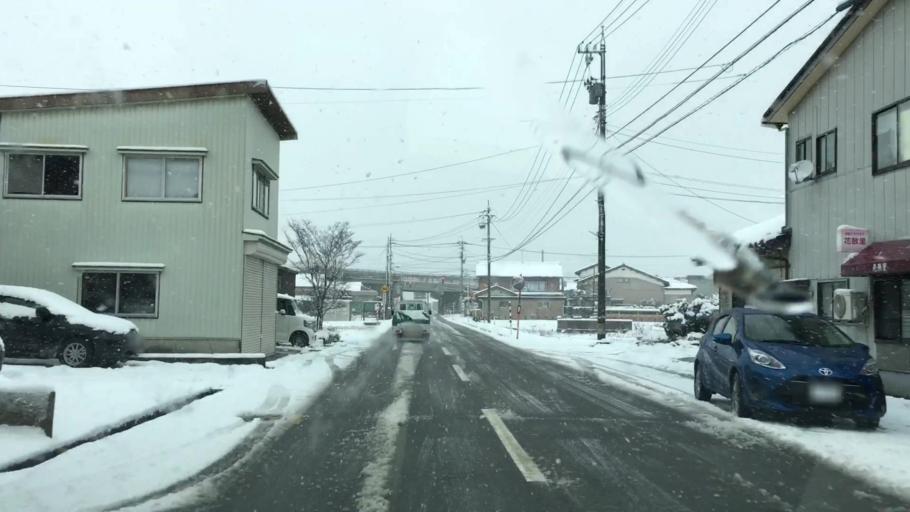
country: JP
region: Toyama
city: Kamiichi
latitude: 36.7008
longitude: 137.3350
